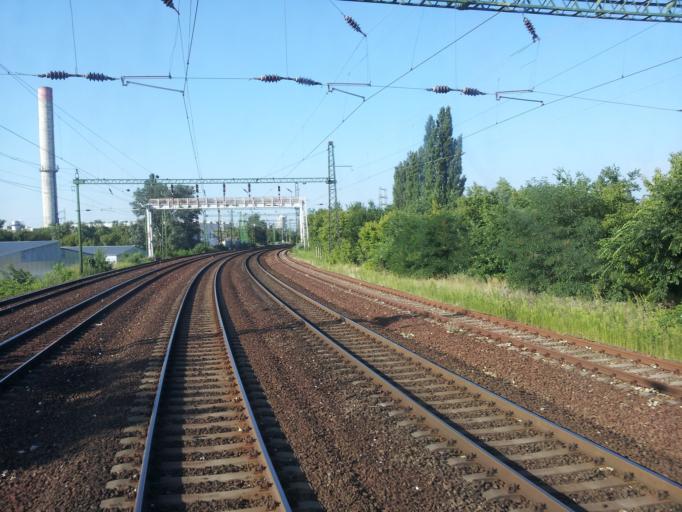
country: HU
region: Budapest
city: Budapest XIV. keruelet
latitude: 47.4804
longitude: 19.1183
